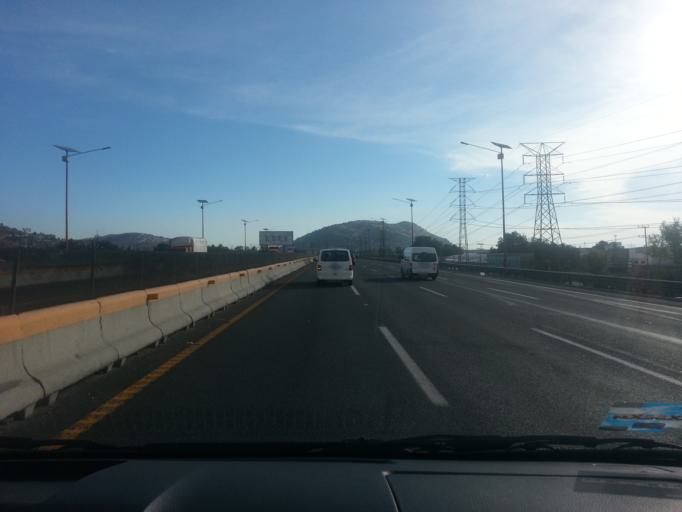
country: MX
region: Mexico
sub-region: Tlalnepantla de Baz
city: Puerto Escondido (Tepeolulco Puerto Escondido)
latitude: 19.5298
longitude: -99.0818
